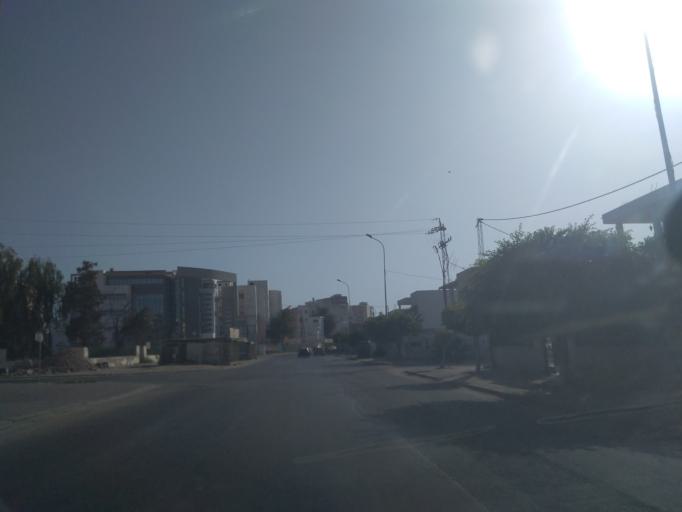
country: TN
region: Safaqis
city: Sfax
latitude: 34.7472
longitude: 10.7677
